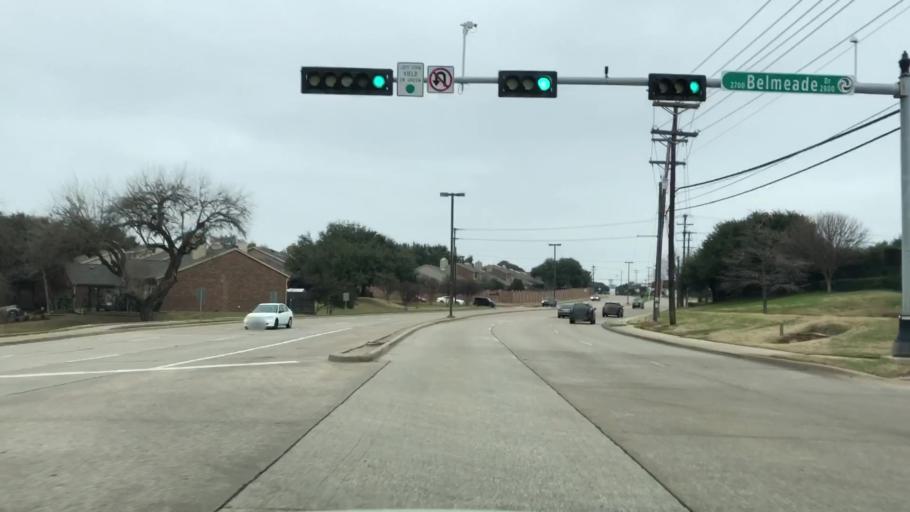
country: US
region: Texas
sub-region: Dallas County
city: Addison
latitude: 32.9807
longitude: -96.8556
